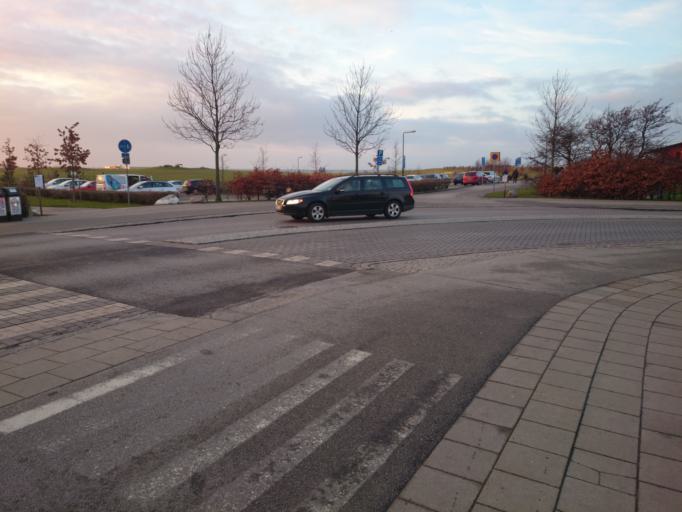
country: SE
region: Skane
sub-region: Malmo
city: Malmoe
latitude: 55.6056
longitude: 12.9790
